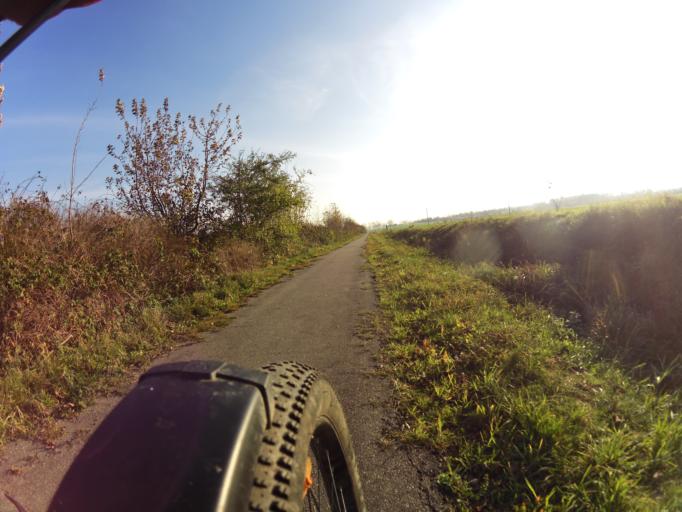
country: PL
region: Pomeranian Voivodeship
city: Strzelno
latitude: 54.7651
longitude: 18.2505
